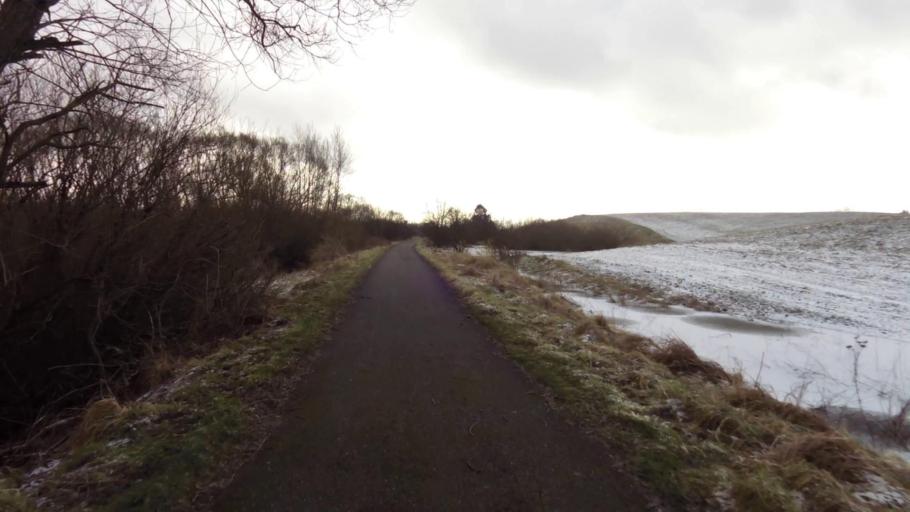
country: PL
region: West Pomeranian Voivodeship
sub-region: Powiat drawski
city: Zlocieniec
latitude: 53.5969
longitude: 16.0473
